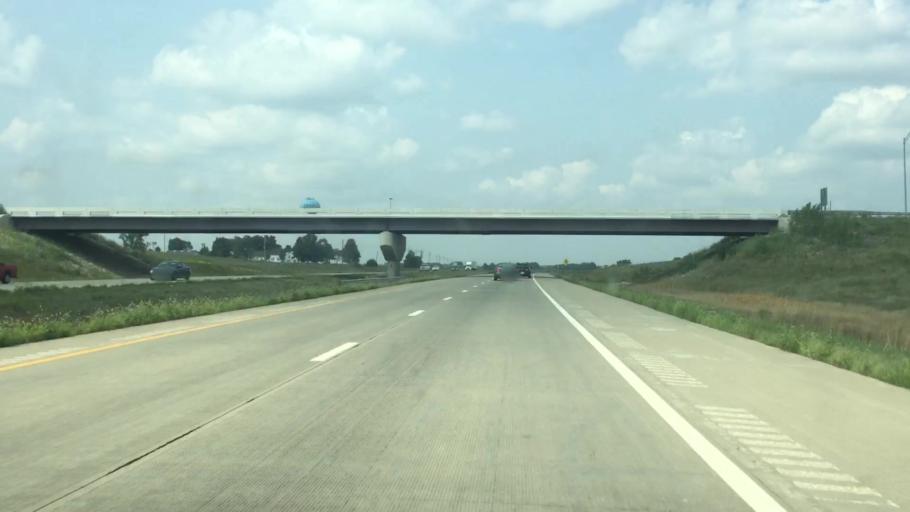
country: US
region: Kansas
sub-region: Douglas County
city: Baldwin City
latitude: 38.8323
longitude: -95.2688
